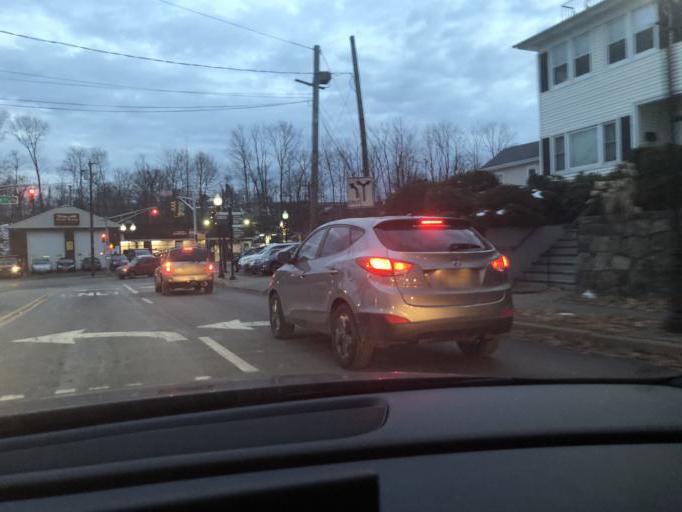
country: US
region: New Jersey
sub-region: Morris County
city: Morristown
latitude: 40.7963
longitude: -74.4715
